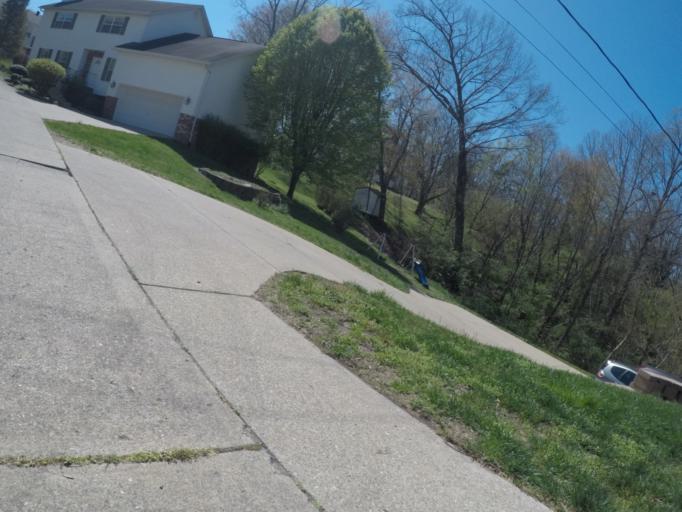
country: US
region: West Virginia
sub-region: Cabell County
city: Pea Ridge
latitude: 38.4170
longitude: -82.3170
